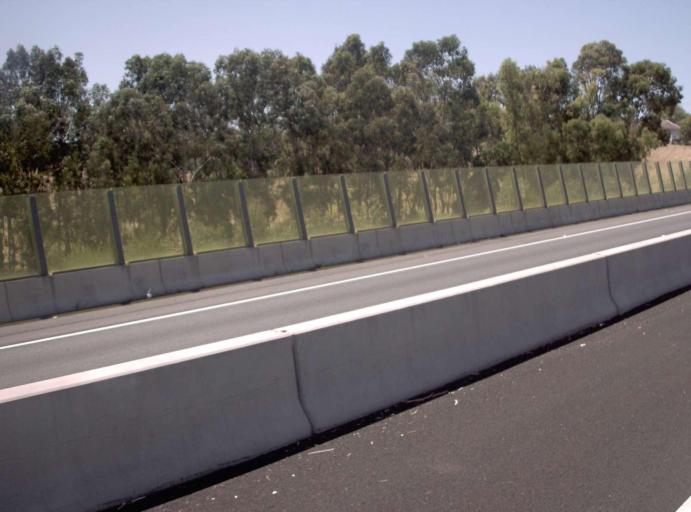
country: AU
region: Victoria
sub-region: Hume
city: Jacana
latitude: -37.6937
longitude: 144.9109
